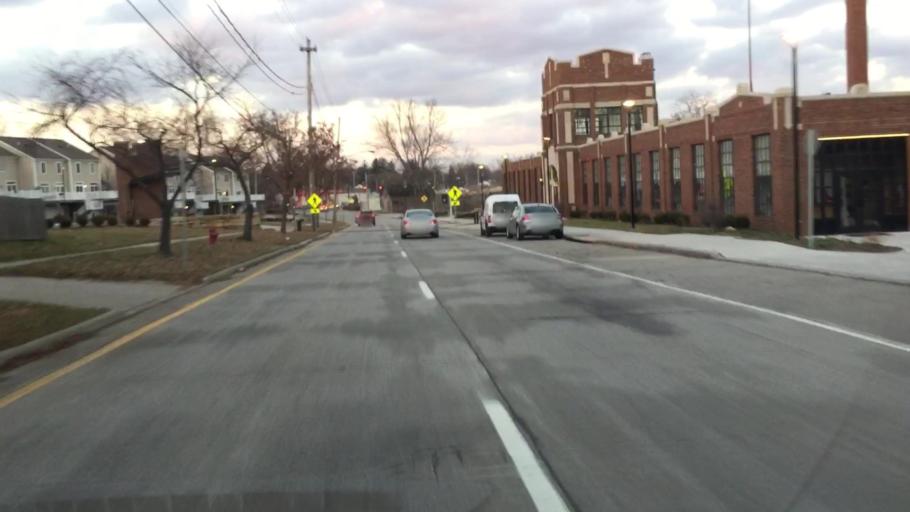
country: US
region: Ohio
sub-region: Portage County
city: Kent
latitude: 41.1558
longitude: -81.3602
